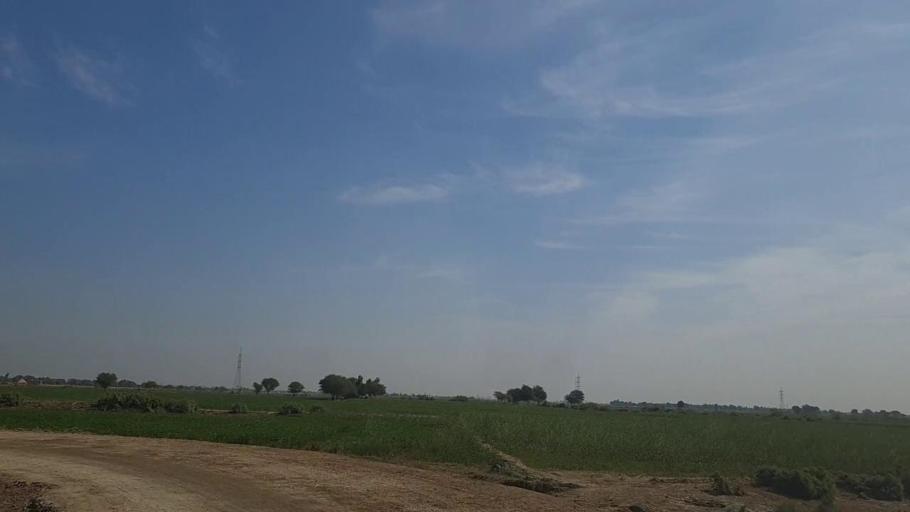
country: PK
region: Sindh
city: Mirpur Khas
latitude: 25.4866
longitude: 68.9658
